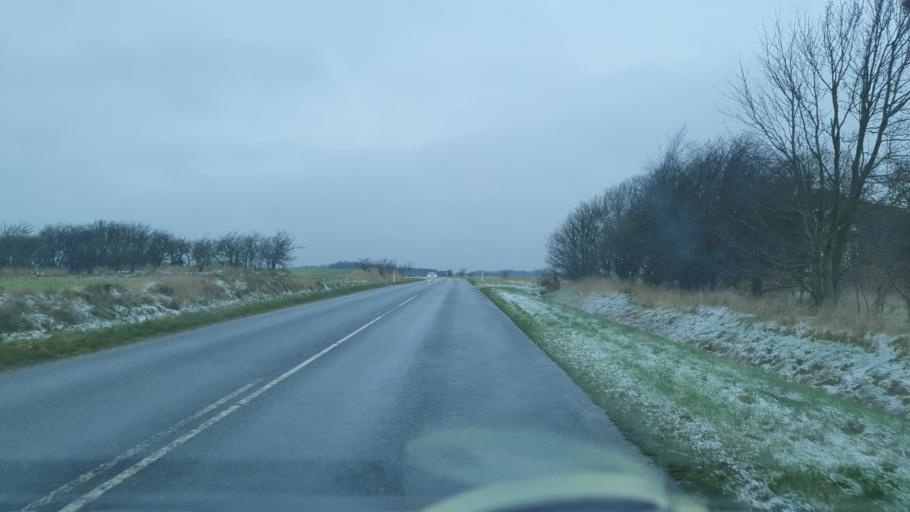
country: DK
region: North Denmark
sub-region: Jammerbugt Kommune
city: Brovst
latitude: 57.1232
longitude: 9.4910
